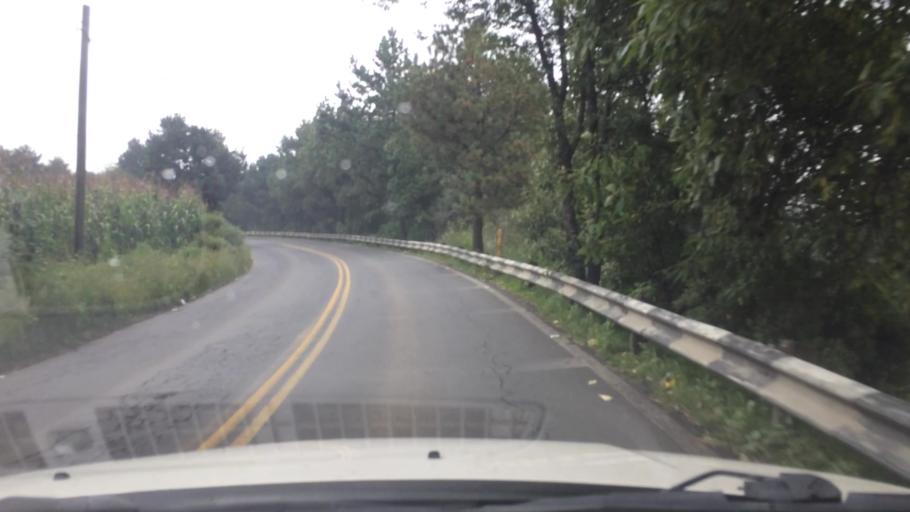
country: MX
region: Mexico City
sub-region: Tlalpan
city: Lomas de Tepemecatl
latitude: 19.2307
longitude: -99.2154
